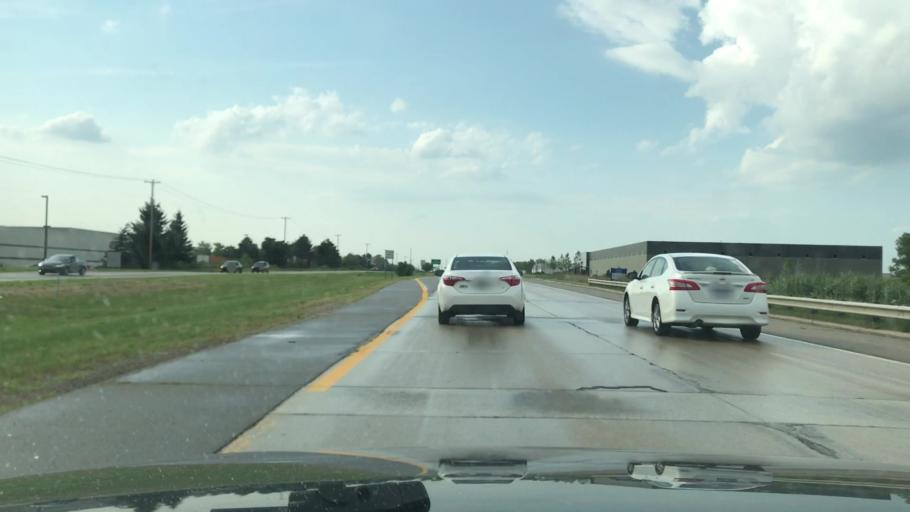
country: US
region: Michigan
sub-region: Kent County
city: Caledonia
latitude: 42.8633
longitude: -85.5489
